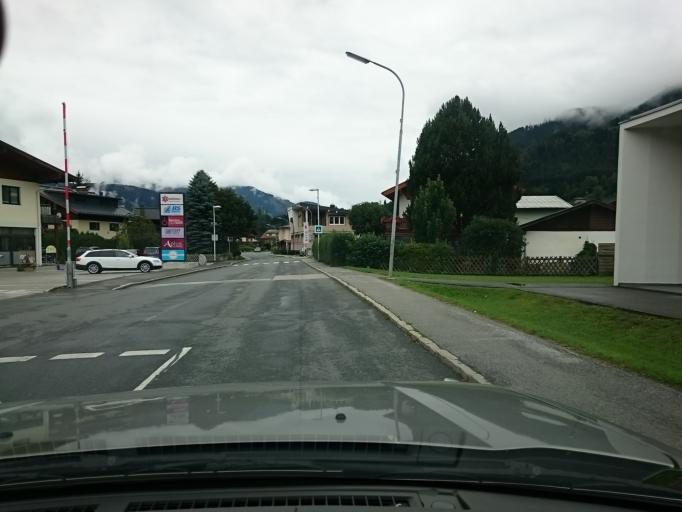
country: AT
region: Salzburg
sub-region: Politischer Bezirk Zell am See
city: Bruck an der Grossglocknerstrasse
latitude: 47.2814
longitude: 12.8246
